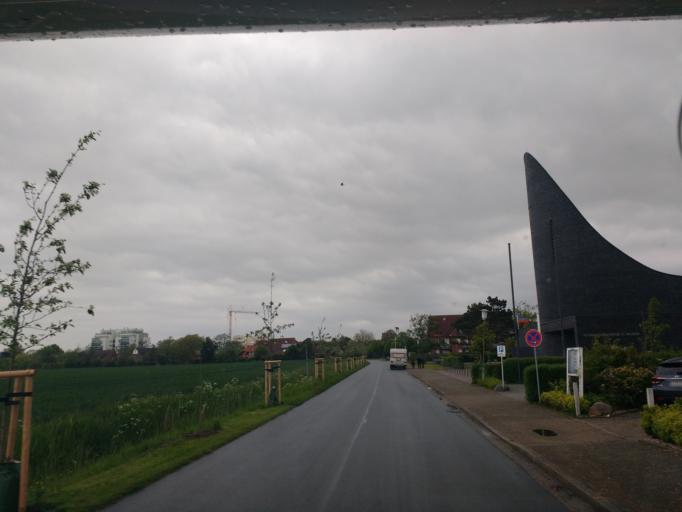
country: DE
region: Lower Saxony
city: Schillig
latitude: 53.7011
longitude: 8.0214
